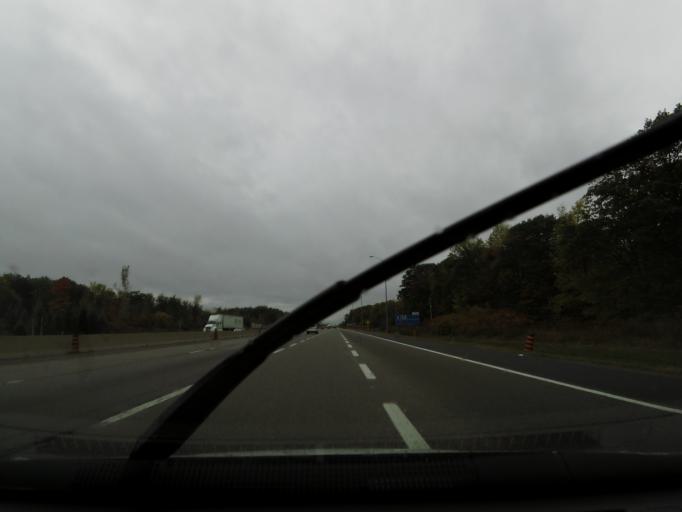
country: CA
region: Ontario
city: Prescott
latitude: 44.7430
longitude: -75.4955
